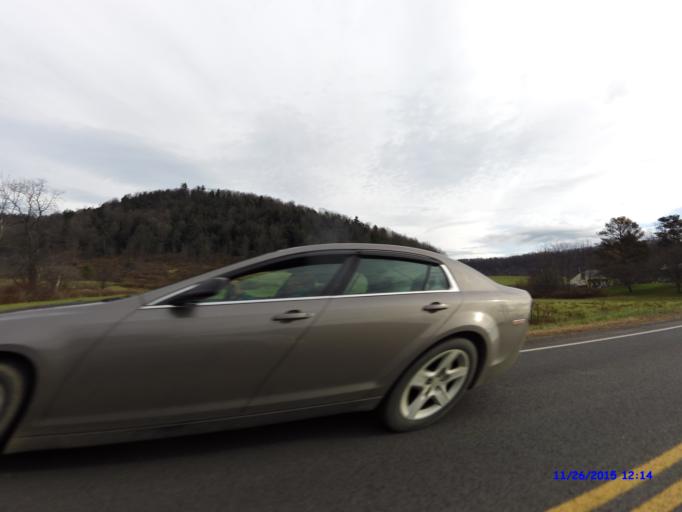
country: US
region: New York
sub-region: Cattaraugus County
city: Allegany
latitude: 42.1395
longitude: -78.5030
